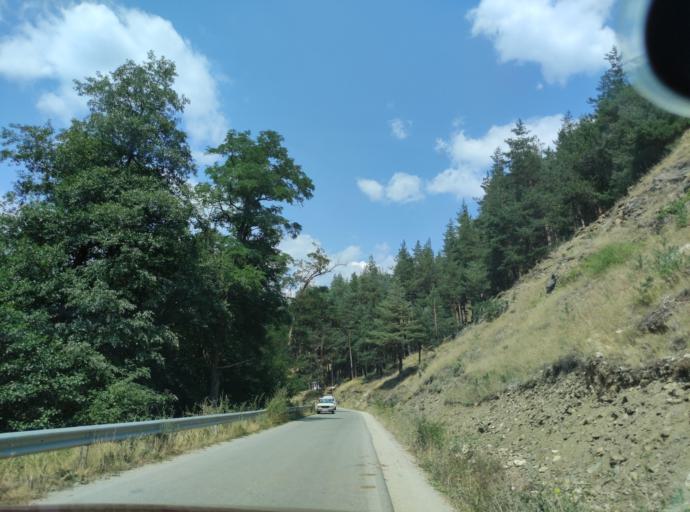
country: BG
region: Blagoevgrad
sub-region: Obshtina Belitsa
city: Belitsa
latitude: 41.9576
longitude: 23.5567
